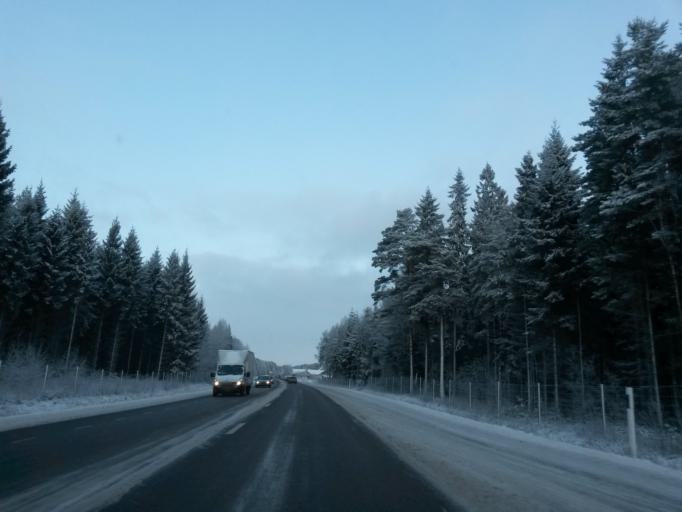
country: SE
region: Vaestra Goetaland
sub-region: Vara Kommun
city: Vara
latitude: 58.1829
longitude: 12.8967
